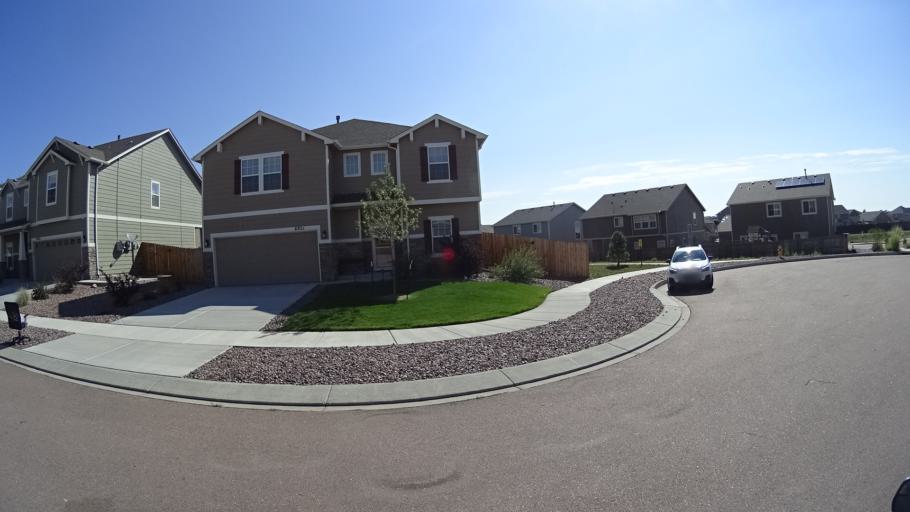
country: US
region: Colorado
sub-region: El Paso County
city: Cimarron Hills
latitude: 38.9325
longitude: -104.6955
